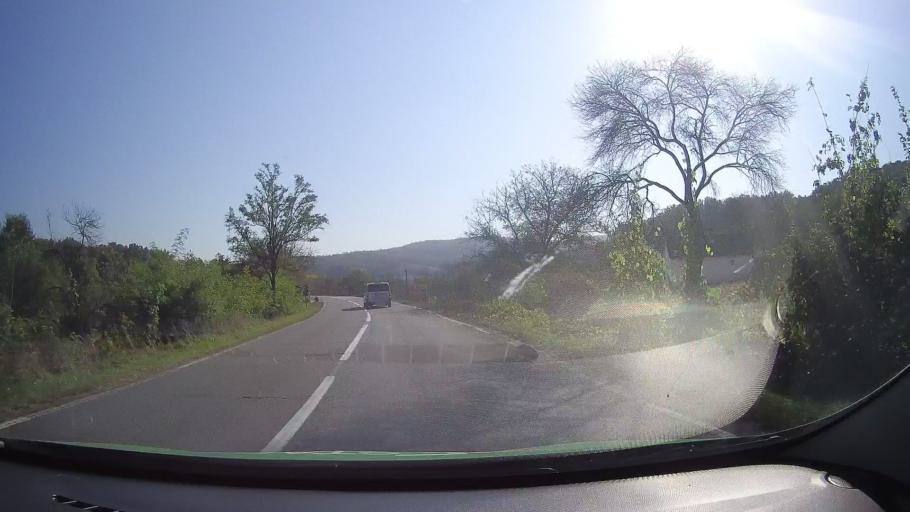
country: RO
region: Hunedoara
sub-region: Comuna Dobra
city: Dobra
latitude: 45.9102
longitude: 22.5312
